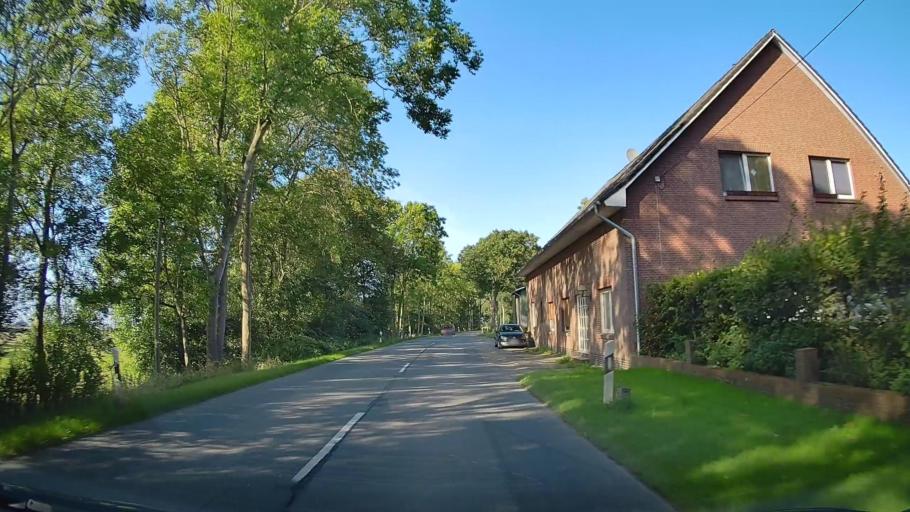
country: DE
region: Lower Saxony
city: Cappel
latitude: 53.7647
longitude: 8.5688
